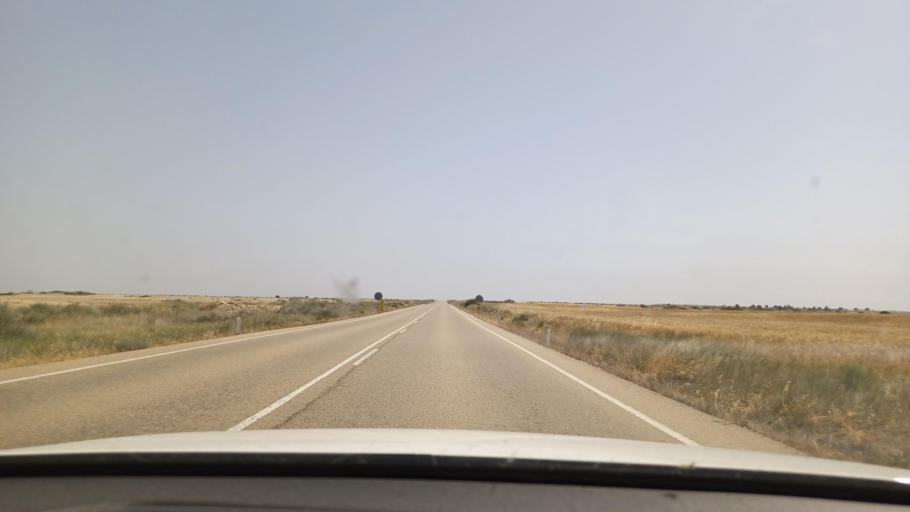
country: ES
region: Aragon
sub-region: Provincia de Zaragoza
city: Bujaraloz
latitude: 41.3846
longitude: -0.1142
